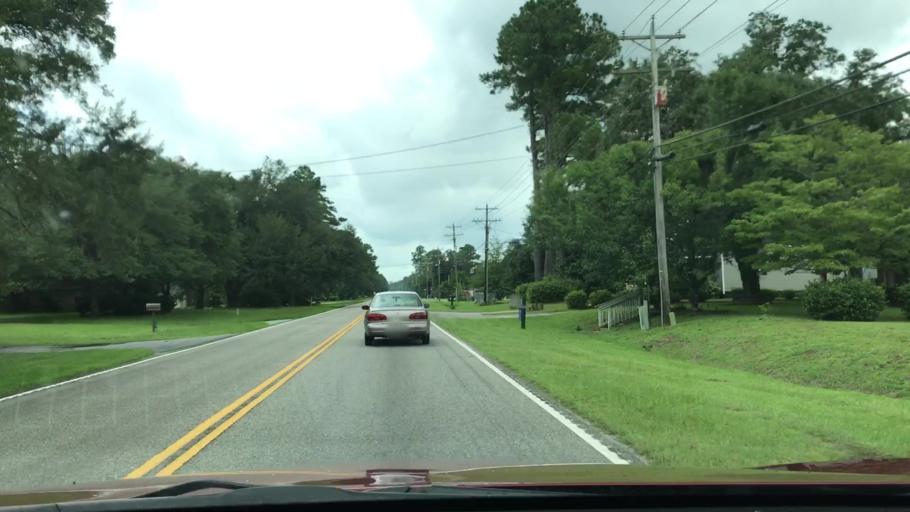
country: US
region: South Carolina
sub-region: Georgetown County
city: Georgetown
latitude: 33.4334
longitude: -79.2775
